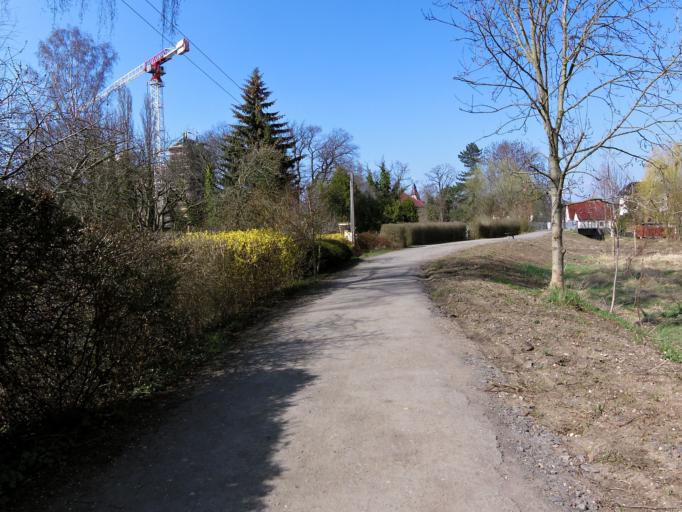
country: DE
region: Saxony
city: Leipzig
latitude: 51.3749
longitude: 12.3020
